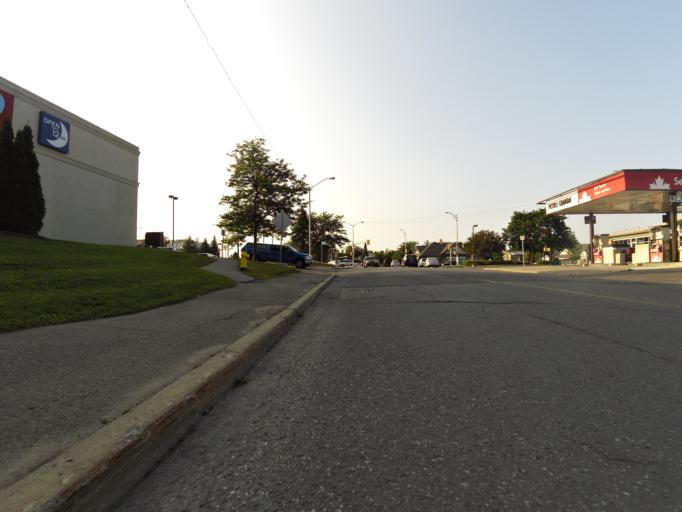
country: CA
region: Ontario
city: Bells Corners
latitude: 45.3019
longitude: -75.8795
